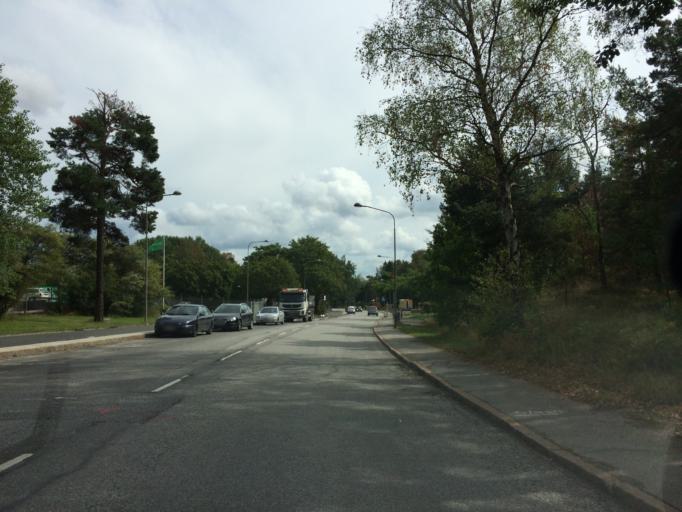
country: SE
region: Stockholm
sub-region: Stockholms Kommun
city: Arsta
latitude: 59.2893
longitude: 18.0031
